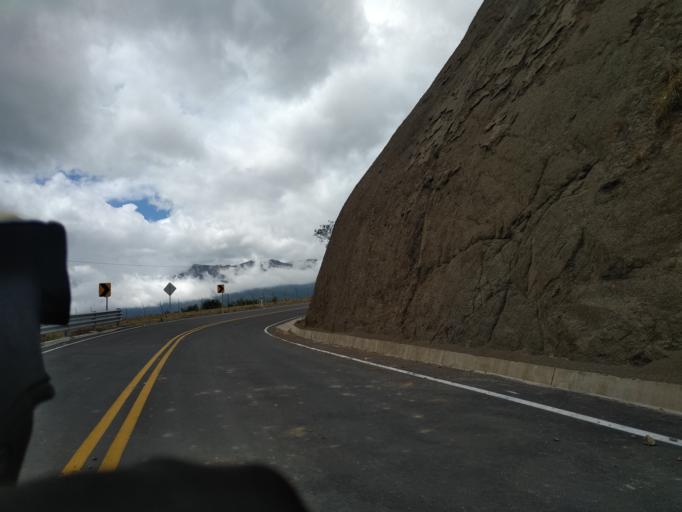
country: EC
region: Cotopaxi
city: Saquisili
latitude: -0.7575
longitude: -78.9136
